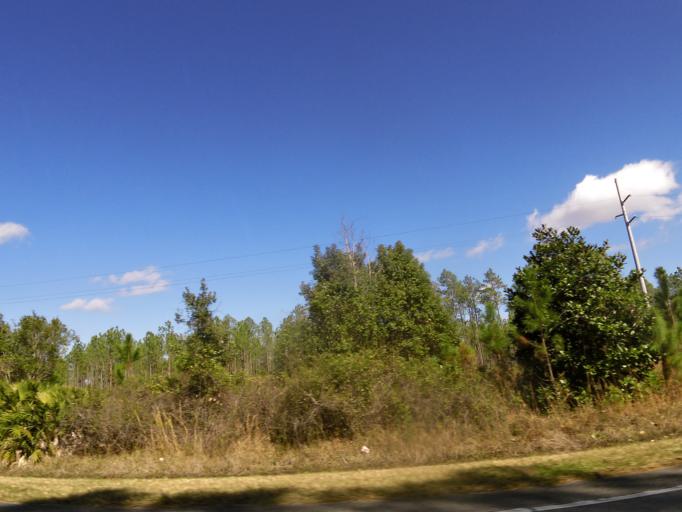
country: US
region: Florida
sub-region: Volusia County
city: De Leon Springs
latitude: 29.1718
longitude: -81.4012
